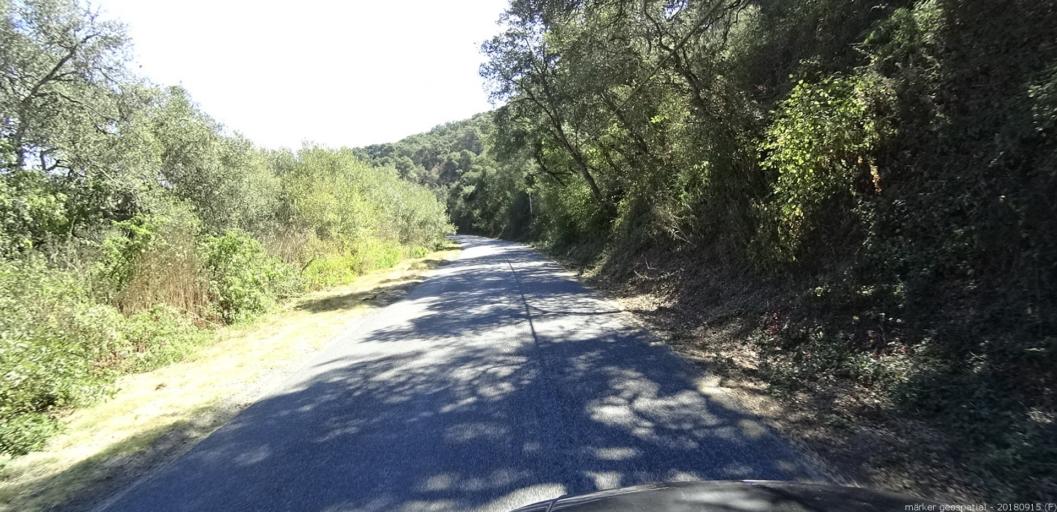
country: US
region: California
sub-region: Monterey County
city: Las Lomas
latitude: 36.8793
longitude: -121.7443
